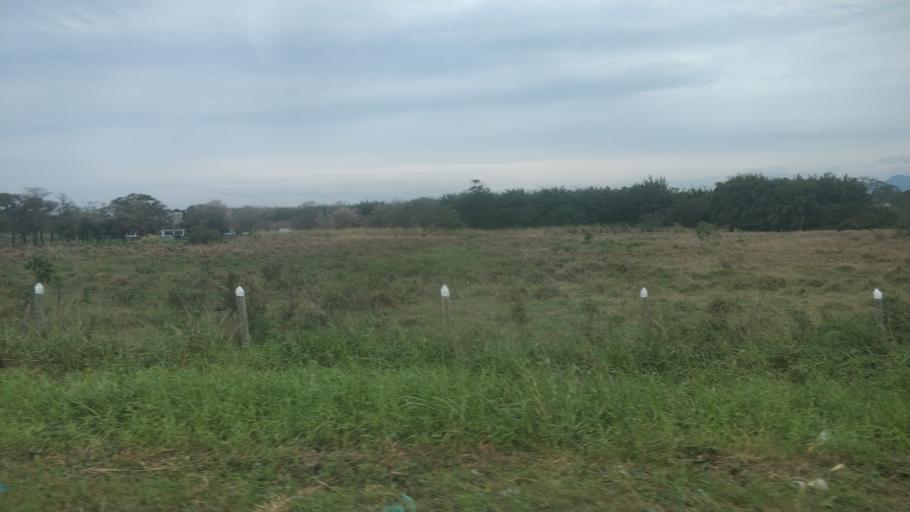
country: BR
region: Rio de Janeiro
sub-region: Seropedica
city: Seropedica
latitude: -22.7728
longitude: -43.6689
